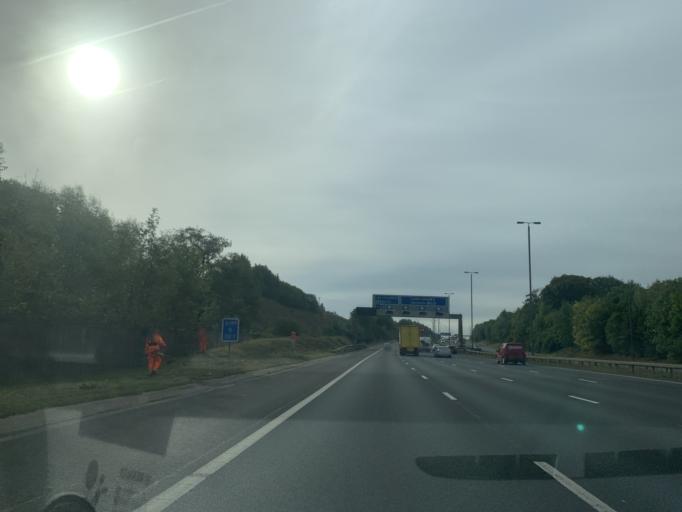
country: GB
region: England
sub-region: City and Borough of Leeds
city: Aberford
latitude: 53.8335
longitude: -1.3383
